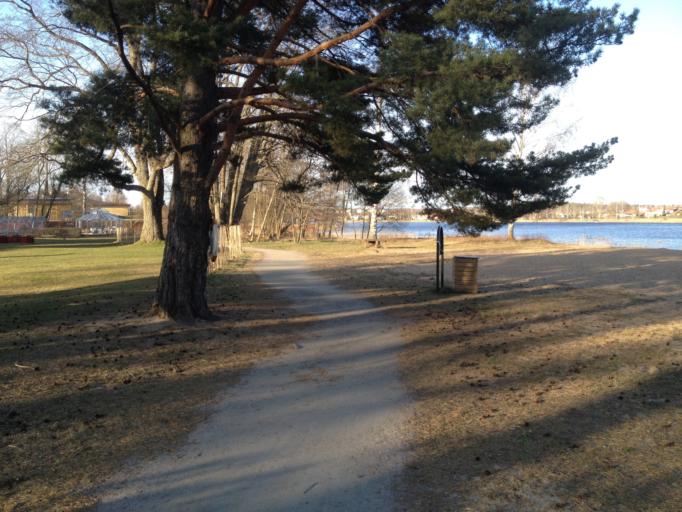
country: SE
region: Vaermland
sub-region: Karlstads Kommun
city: Karlstad
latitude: 59.3891
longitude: 13.4967
